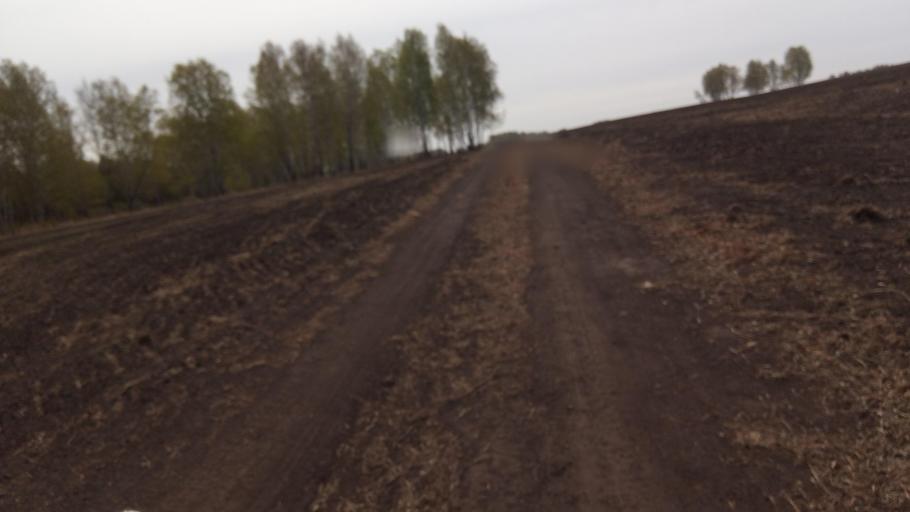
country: RU
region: Chelyabinsk
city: Timiryazevskiy
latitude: 55.0207
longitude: 60.8524
